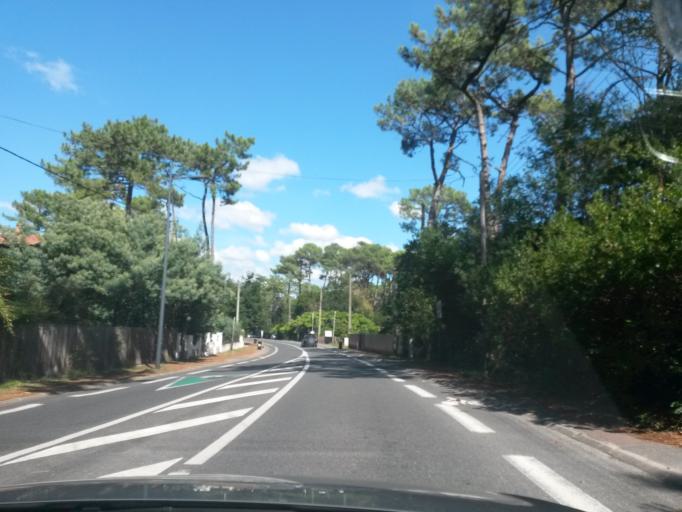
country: FR
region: Aquitaine
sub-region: Departement de la Gironde
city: Arcachon
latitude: 44.7115
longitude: -1.2198
